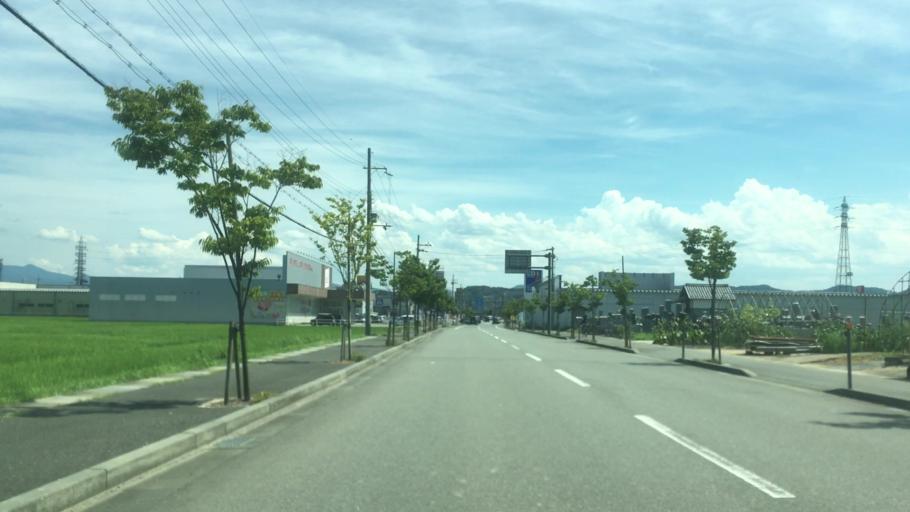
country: JP
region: Hyogo
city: Toyooka
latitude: 35.5573
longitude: 134.8155
